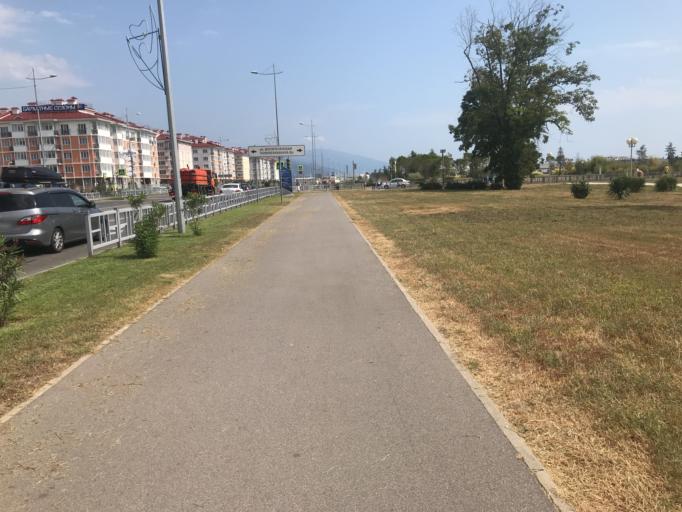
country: RU
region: Krasnodarskiy
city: Adler
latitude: 43.4007
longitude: 39.9760
